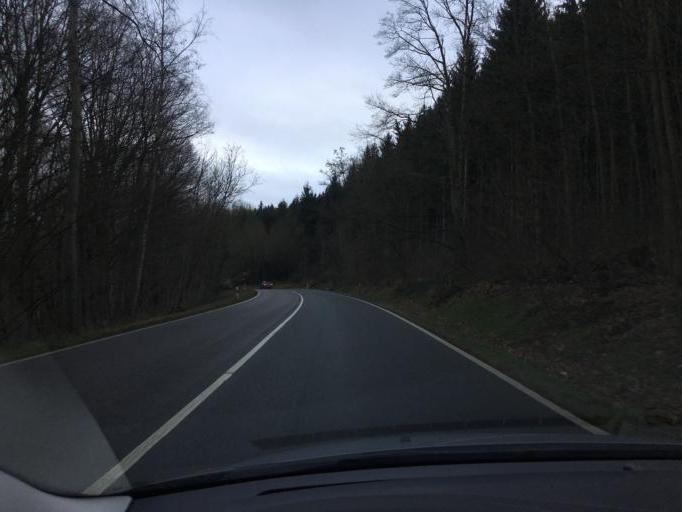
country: DE
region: Saxony
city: Waldenburg
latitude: 50.8871
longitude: 12.6214
